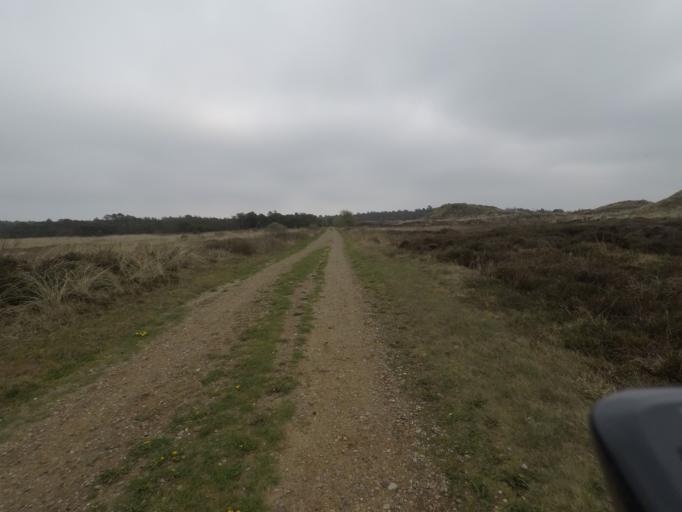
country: DE
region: Schleswig-Holstein
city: List
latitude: 55.1177
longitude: 8.5218
